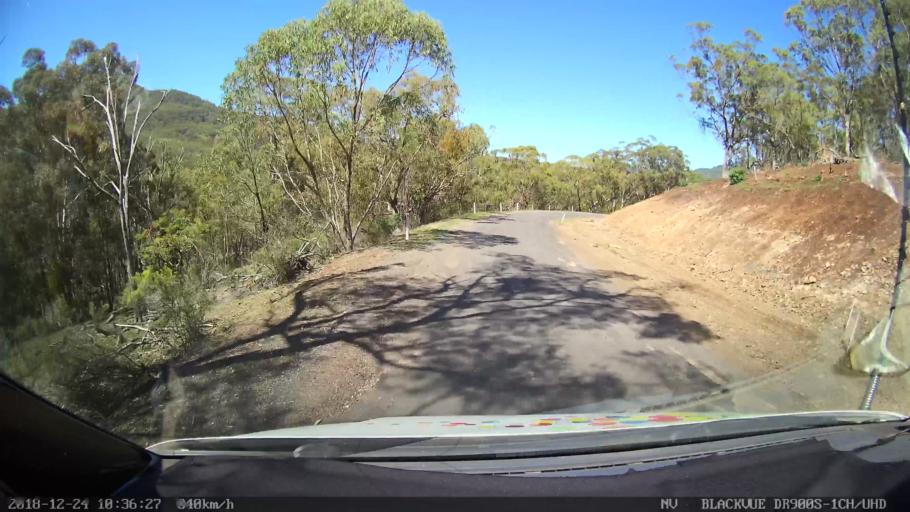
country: AU
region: New South Wales
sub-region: Upper Hunter Shire
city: Merriwa
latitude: -31.8445
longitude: 150.4999
